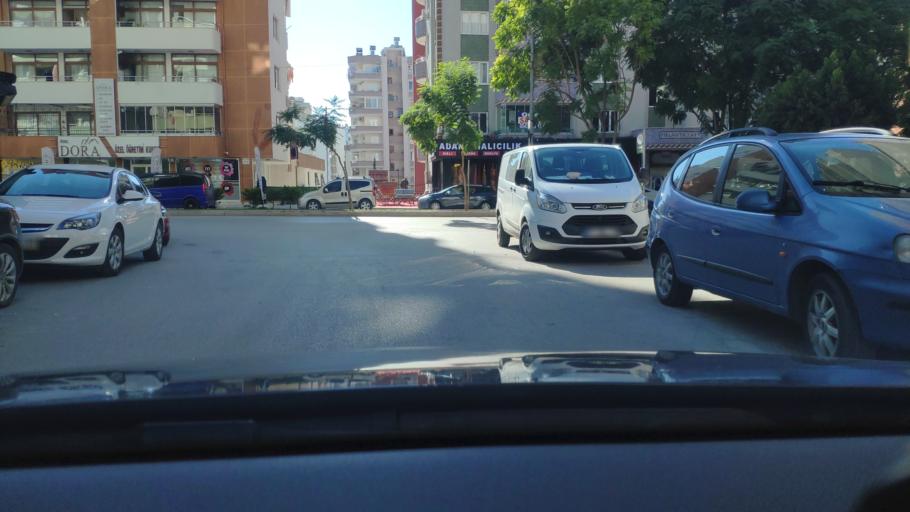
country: TR
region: Adana
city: Adana
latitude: 37.0531
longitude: 35.2815
